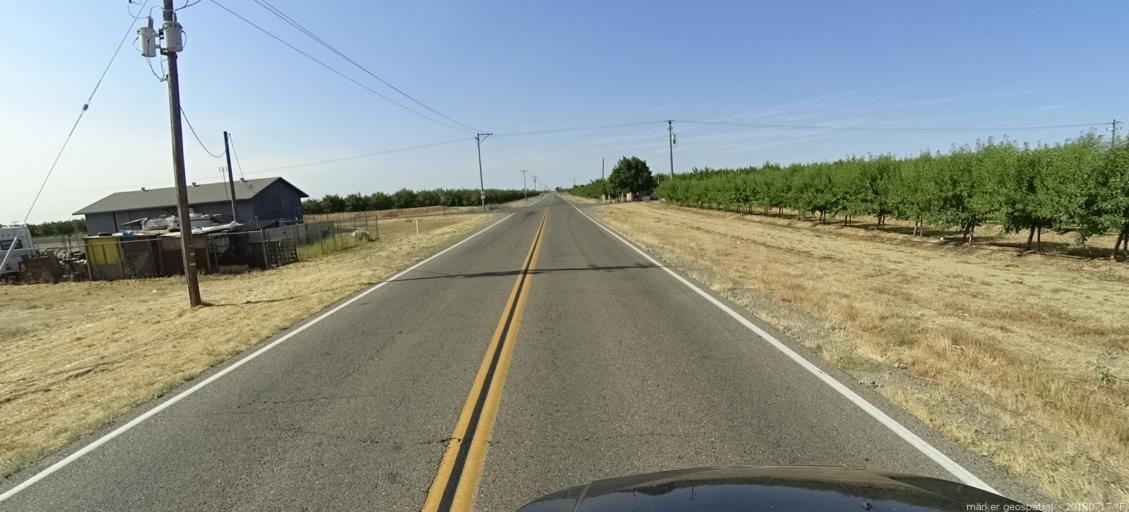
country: US
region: California
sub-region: Madera County
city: Madera Acres
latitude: 37.0263
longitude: -120.1107
